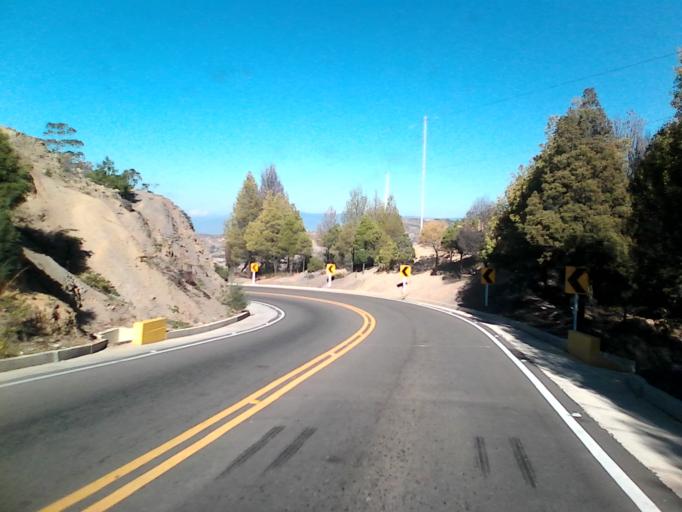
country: CO
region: Boyaca
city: Cucaita
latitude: 5.5487
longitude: -73.4408
